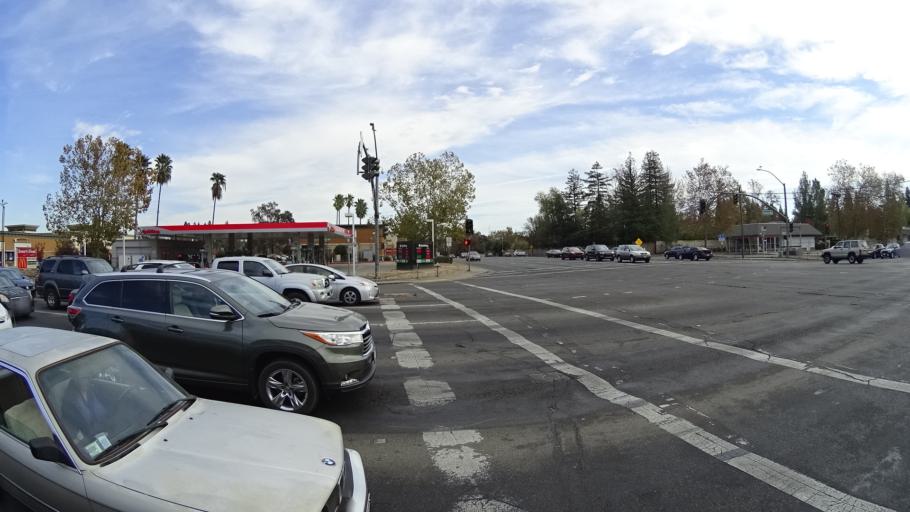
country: US
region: California
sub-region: Sacramento County
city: Fair Oaks
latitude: 38.6641
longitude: -121.2722
